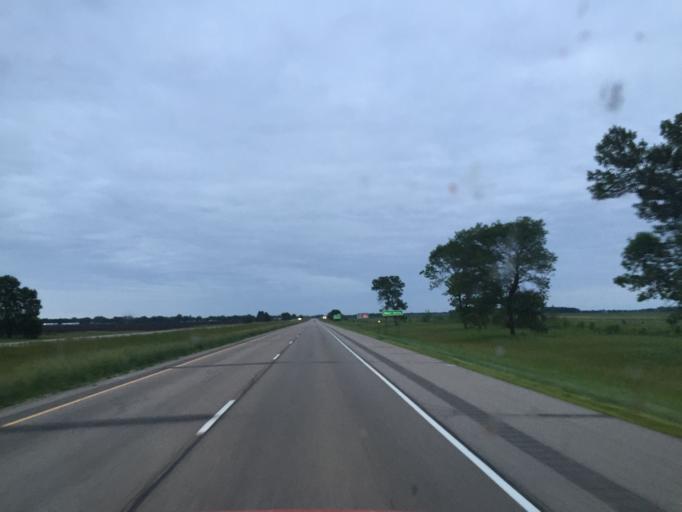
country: US
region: Minnesota
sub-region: Mower County
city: Austin
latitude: 43.6596
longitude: -93.0501
